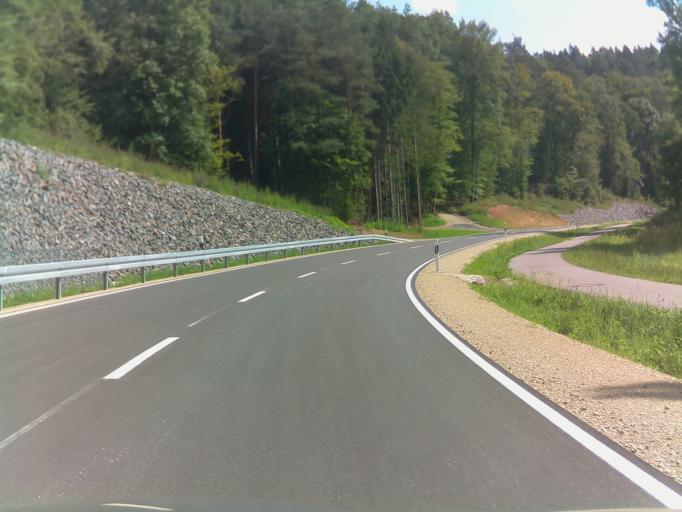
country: DE
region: Bavaria
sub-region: Regierungsbezirk Unterfranken
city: Breitbrunn
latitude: 50.0039
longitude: 10.6892
